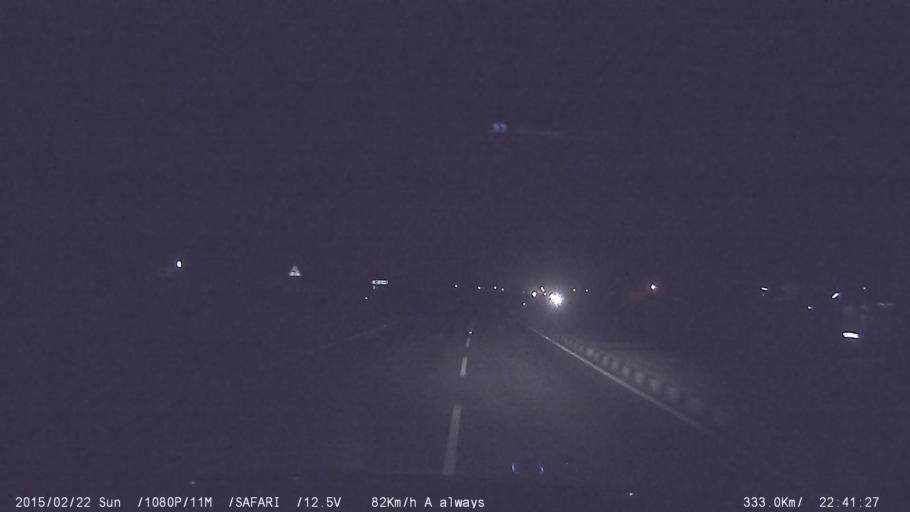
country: IN
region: Tamil Nadu
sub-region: Namakkal
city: Namakkal
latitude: 11.1837
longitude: 78.0709
